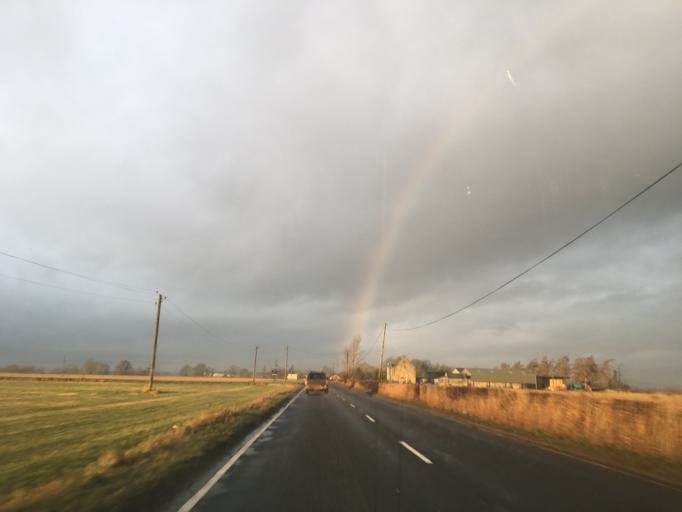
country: GB
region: Scotland
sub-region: Clackmannanshire
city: Alloa
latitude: 56.0971
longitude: -3.8237
